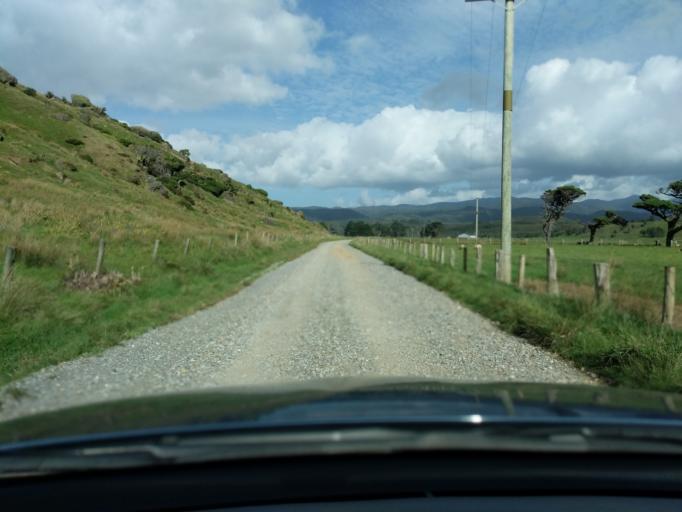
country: NZ
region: Tasman
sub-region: Tasman District
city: Takaka
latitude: -40.6505
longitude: 172.4409
